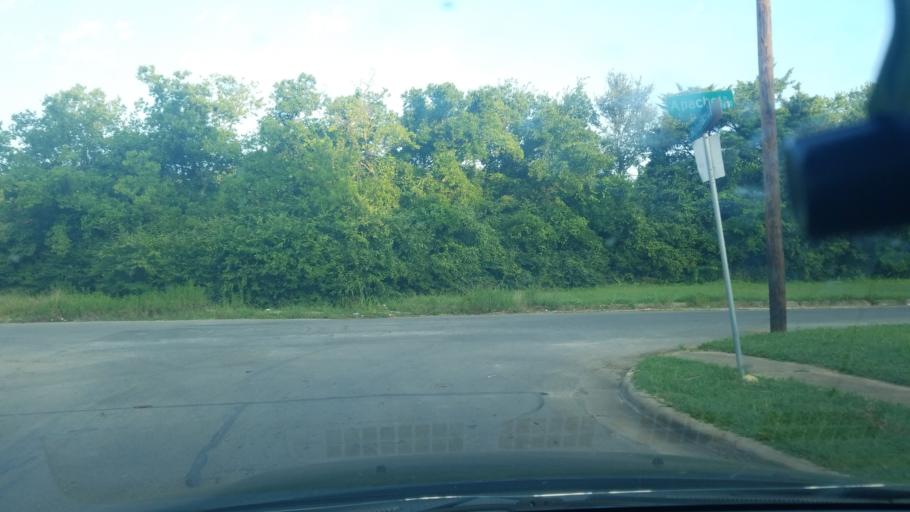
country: US
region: Texas
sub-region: Dallas County
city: Balch Springs
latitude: 32.7246
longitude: -96.6524
